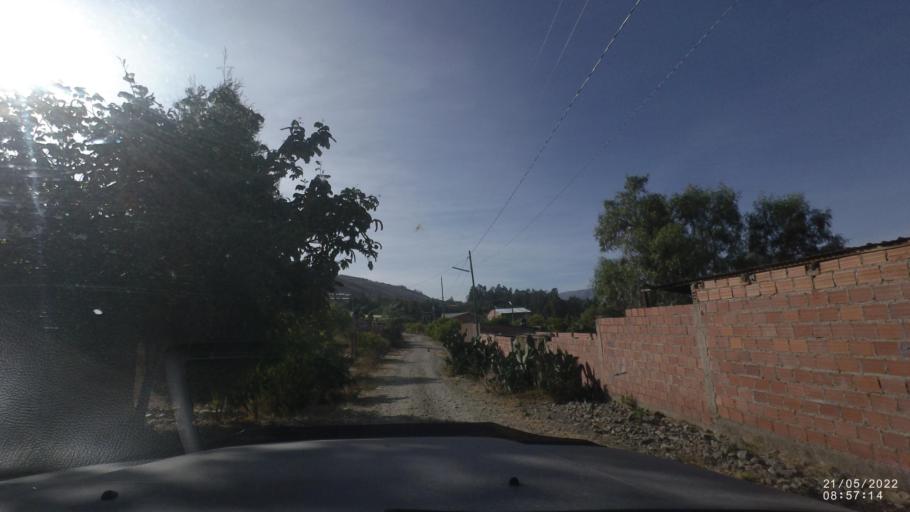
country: BO
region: Cochabamba
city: Cochabamba
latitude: -17.3783
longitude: -66.0405
